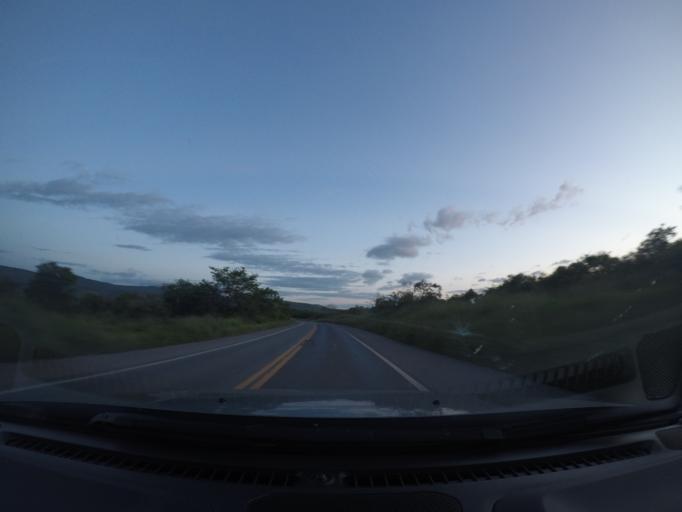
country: BR
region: Bahia
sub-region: Seabra
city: Seabra
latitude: -12.4818
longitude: -41.7385
